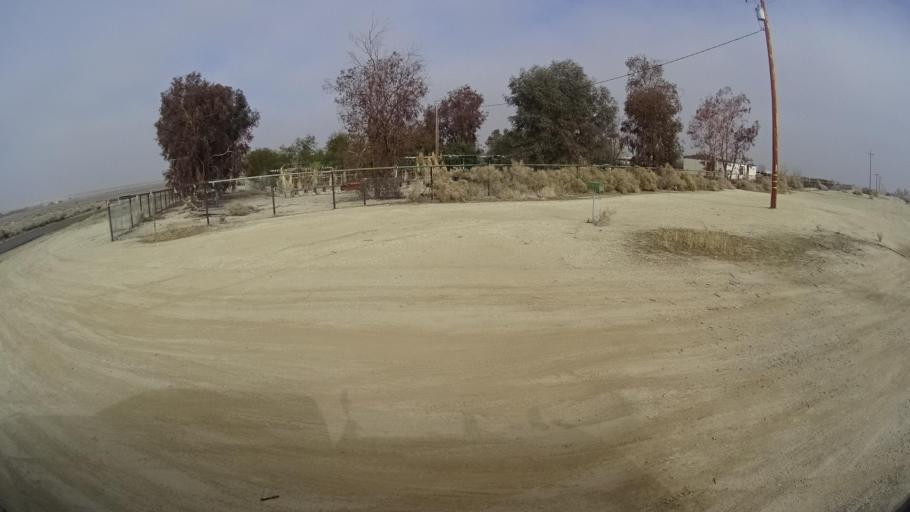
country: US
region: California
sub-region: Kern County
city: Maricopa
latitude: 35.0469
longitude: -119.3668
